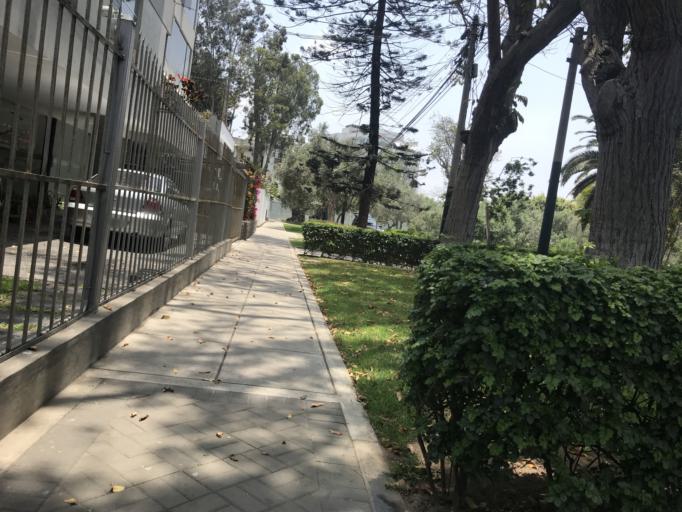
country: PE
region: Lima
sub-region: Lima
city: San Isidro
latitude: -12.0974
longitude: -77.0340
